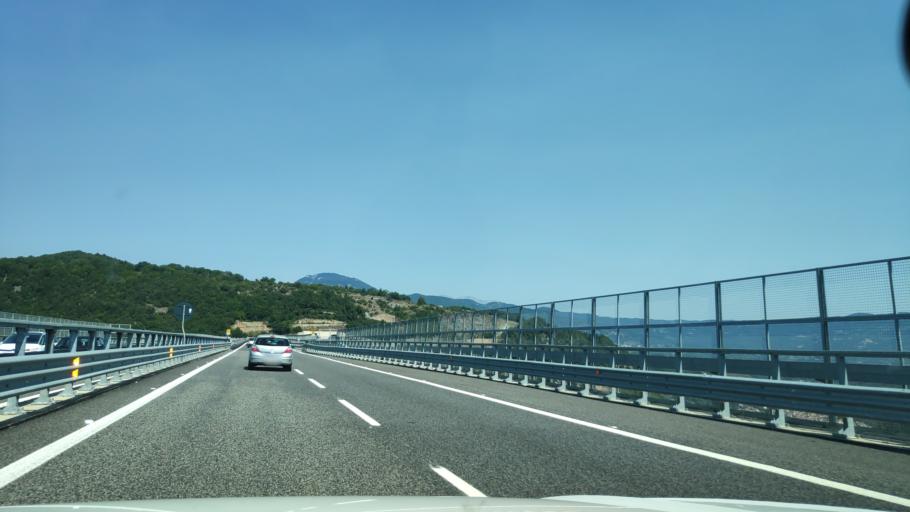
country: IT
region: Calabria
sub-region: Provincia di Cosenza
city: Laino Castello-Nuovo Centro
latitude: 39.9364
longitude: 15.9603
